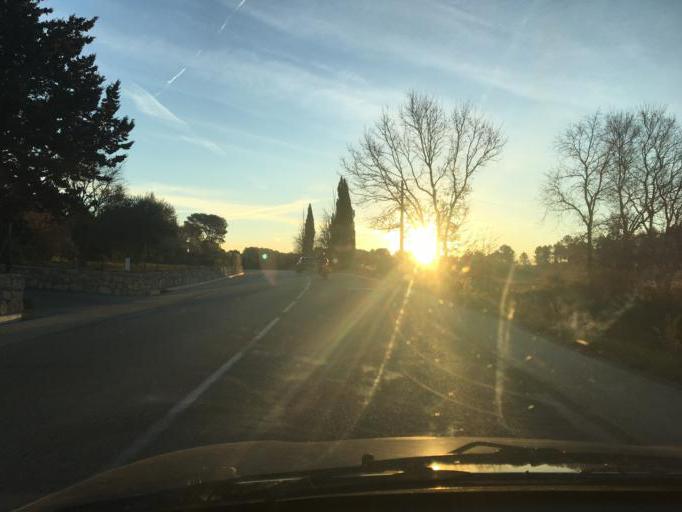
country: FR
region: Provence-Alpes-Cote d'Azur
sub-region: Departement du Var
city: Taradeau
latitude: 43.4652
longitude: 6.3946
